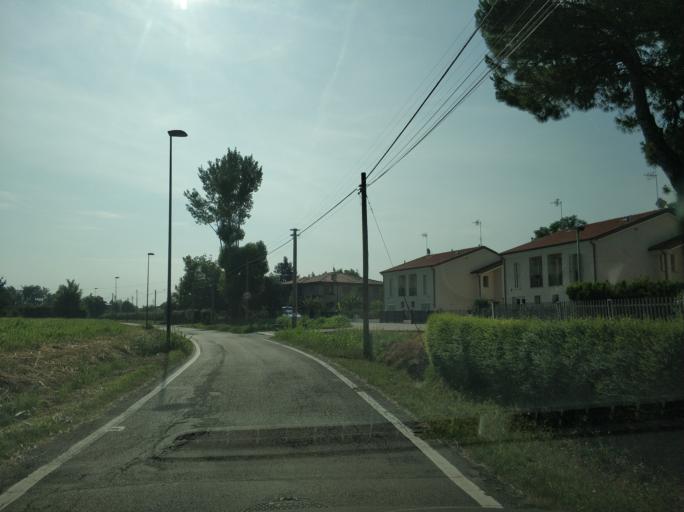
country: IT
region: Veneto
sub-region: Provincia di Padova
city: Este
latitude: 45.2229
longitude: 11.6750
